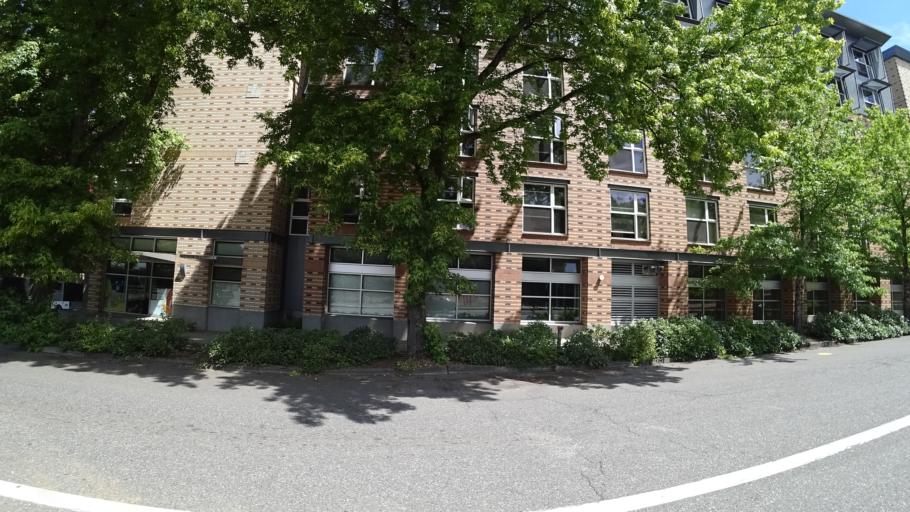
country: US
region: Oregon
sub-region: Multnomah County
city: Portland
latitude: 45.5130
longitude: -122.6882
